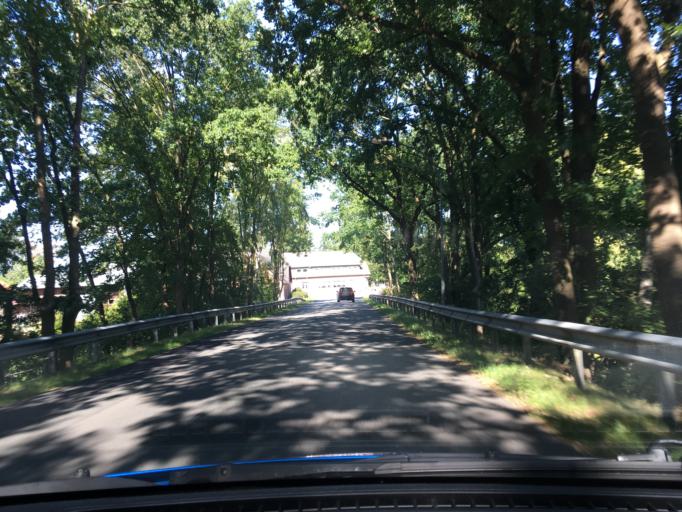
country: DE
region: Lower Saxony
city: Hermannsburg
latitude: 52.8606
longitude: 10.0498
